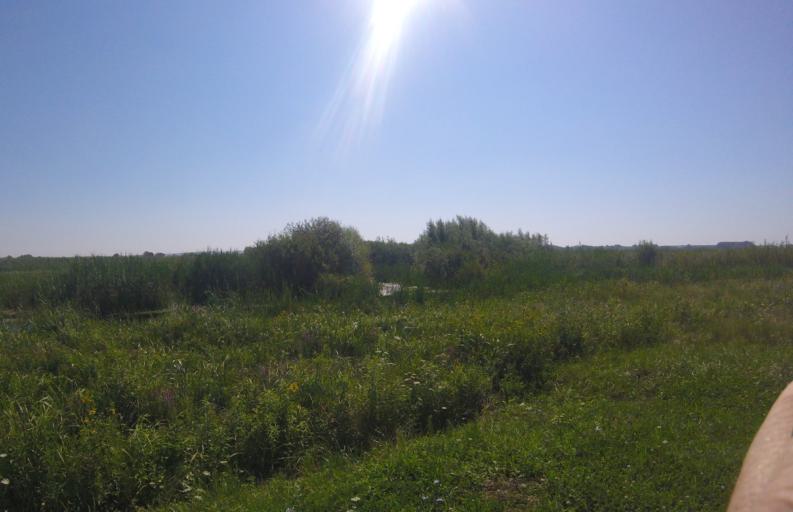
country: HU
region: Zala
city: Sarmellek
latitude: 46.6806
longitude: 17.2372
